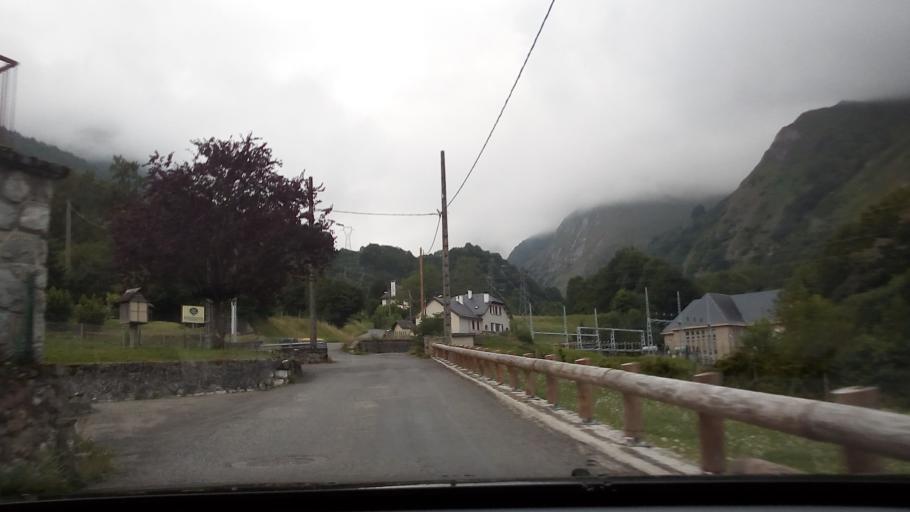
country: FR
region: Midi-Pyrenees
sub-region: Departement des Hautes-Pyrenees
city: Cauterets
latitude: 42.9474
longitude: -0.2170
